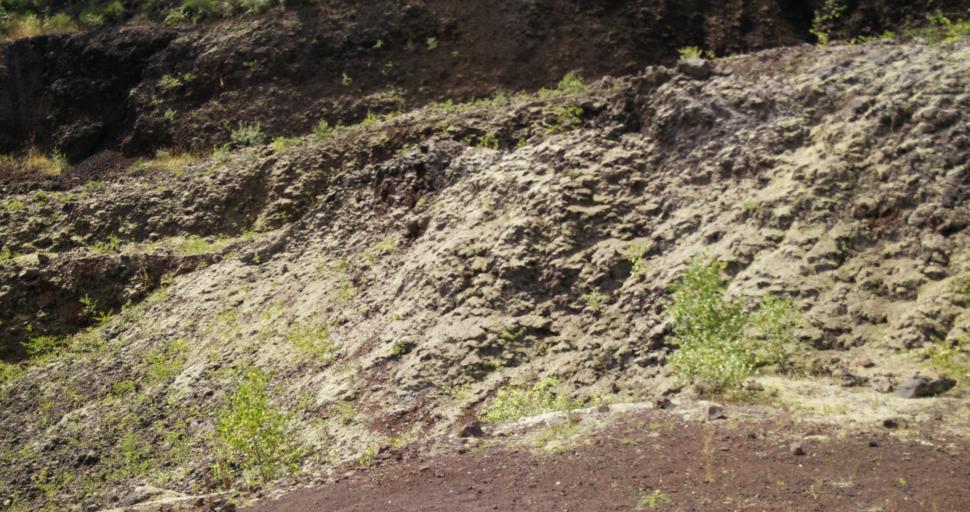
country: FR
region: Auvergne
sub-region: Departement du Puy-de-Dome
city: Saint-Ours
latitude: 45.8180
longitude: 2.9451
